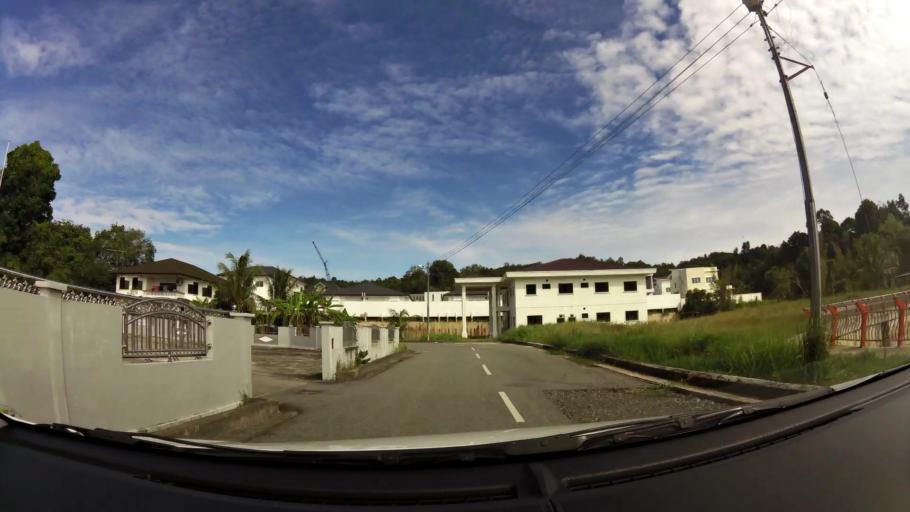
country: BN
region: Brunei and Muara
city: Bandar Seri Begawan
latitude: 4.9092
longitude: 114.9815
